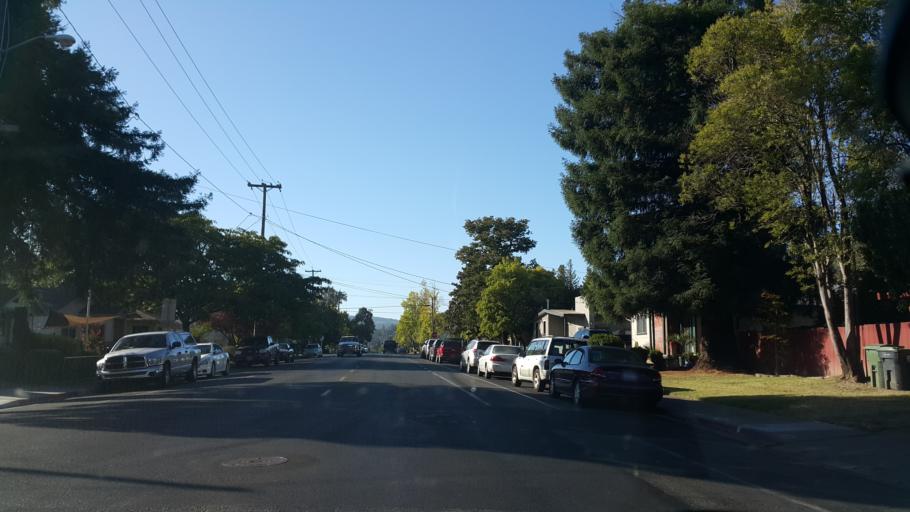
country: US
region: California
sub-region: Mendocino County
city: Ukiah
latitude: 39.1381
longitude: -123.2100
